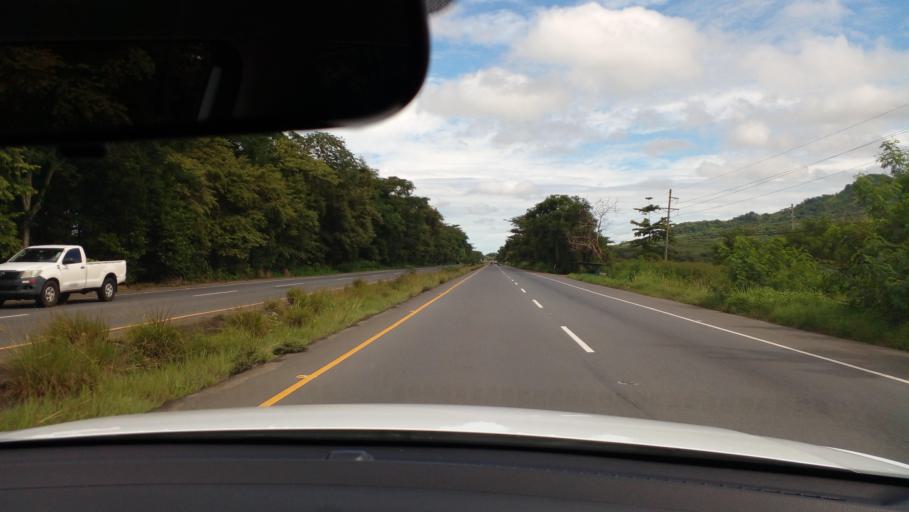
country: PA
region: Cocle
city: El Cano
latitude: 8.3759
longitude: -80.5297
